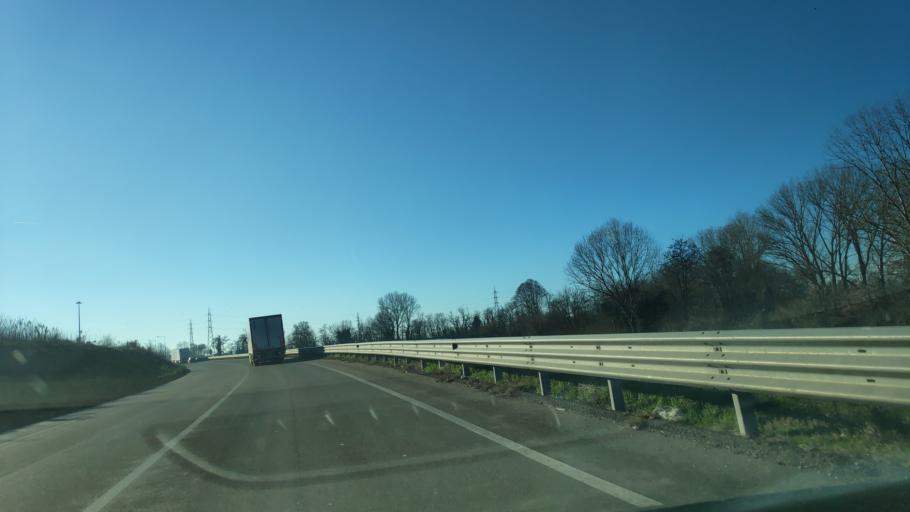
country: IT
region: Lombardy
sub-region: Citta metropolitana di Milano
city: Melegnano
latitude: 45.3671
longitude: 9.3234
